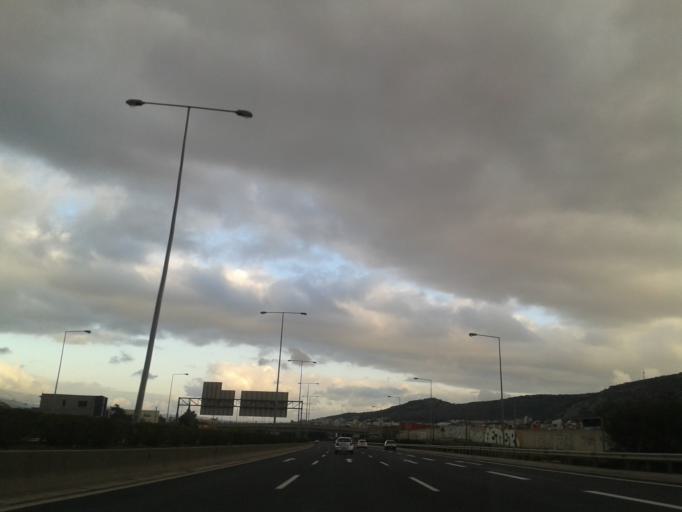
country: GR
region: Attica
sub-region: Nomarchia Dytikis Attikis
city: Ano Liosia
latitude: 38.0759
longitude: 23.6817
